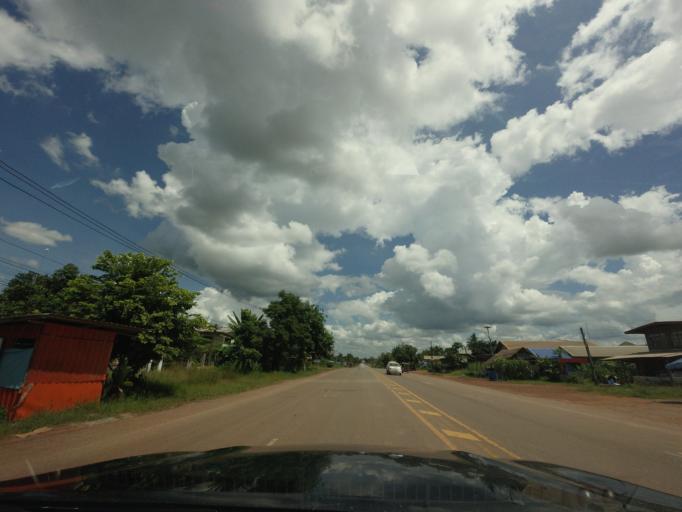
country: TH
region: Changwat Udon Thani
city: Ban Dung
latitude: 17.6795
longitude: 103.2360
